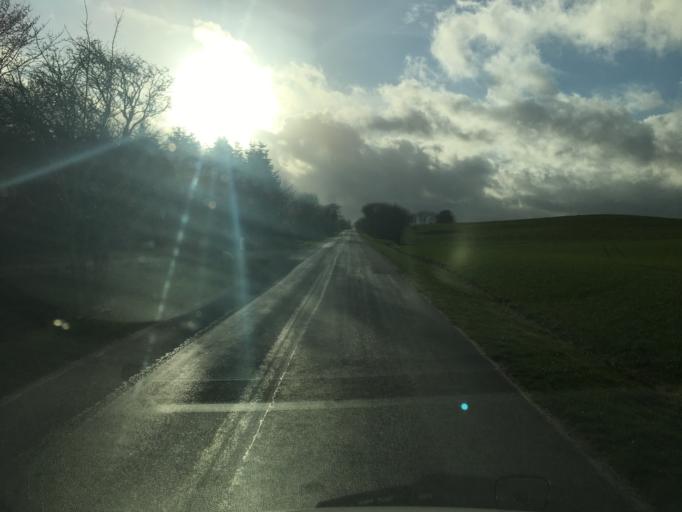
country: DK
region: South Denmark
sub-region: Sonderborg Kommune
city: Grasten
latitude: 54.9641
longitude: 9.5566
